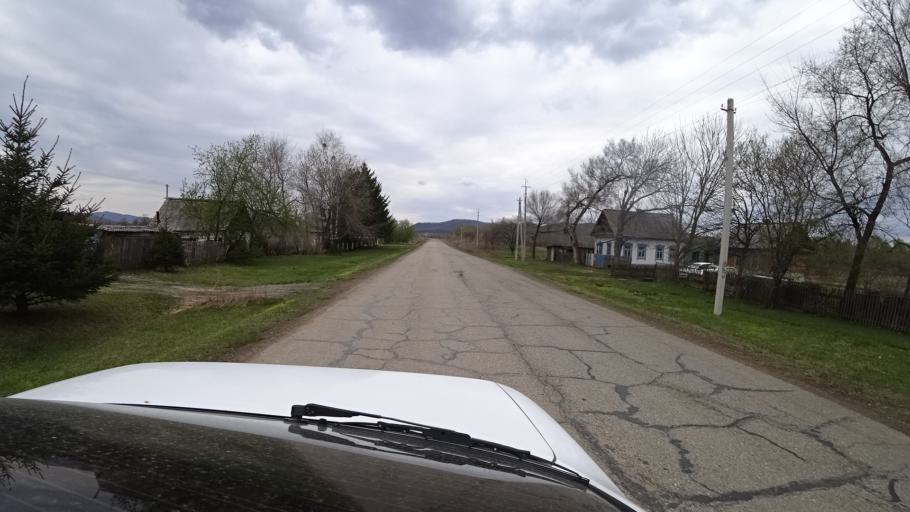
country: RU
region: Primorskiy
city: Novopokrovka
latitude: 45.5523
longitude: 134.3612
